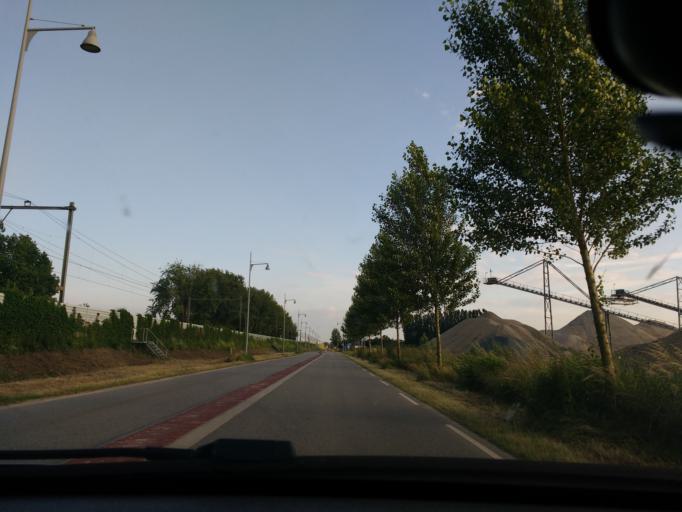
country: NL
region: Gelderland
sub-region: Gemeente Overbetuwe
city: Oosterhout
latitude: 51.8749
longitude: 5.8584
